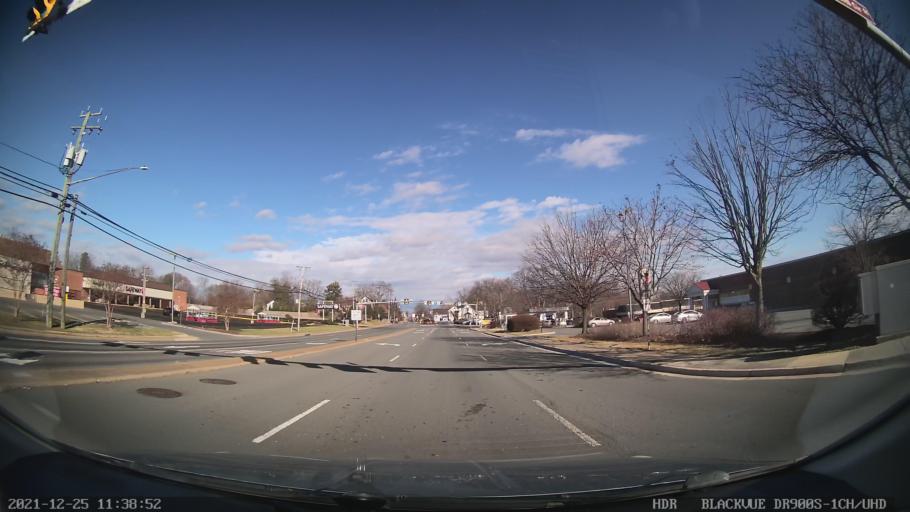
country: US
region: Virginia
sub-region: Loudoun County
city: Leesburg
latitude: 39.1079
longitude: -77.5680
